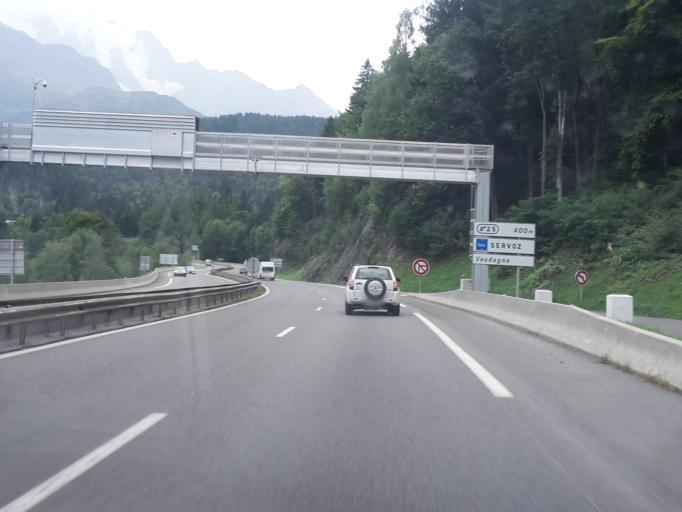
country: FR
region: Rhone-Alpes
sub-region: Departement de la Haute-Savoie
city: Les Houches
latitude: 45.9194
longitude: 6.7631
